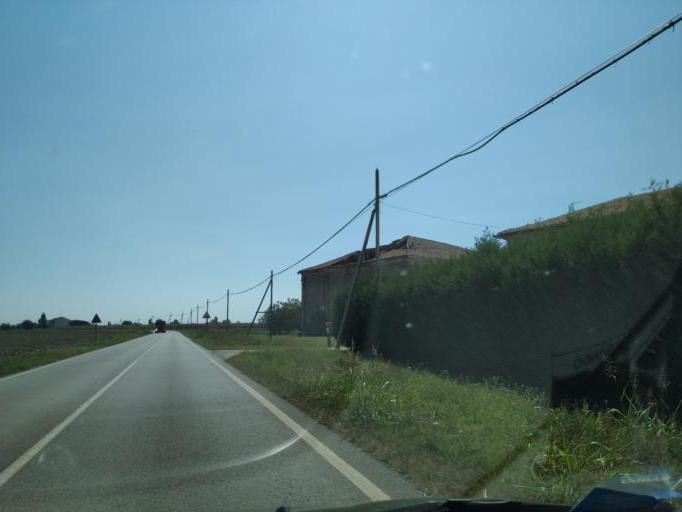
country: IT
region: Emilia-Romagna
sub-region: Provincia di Ferrara
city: Coccanile-Cesta
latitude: 44.8850
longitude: 11.8616
